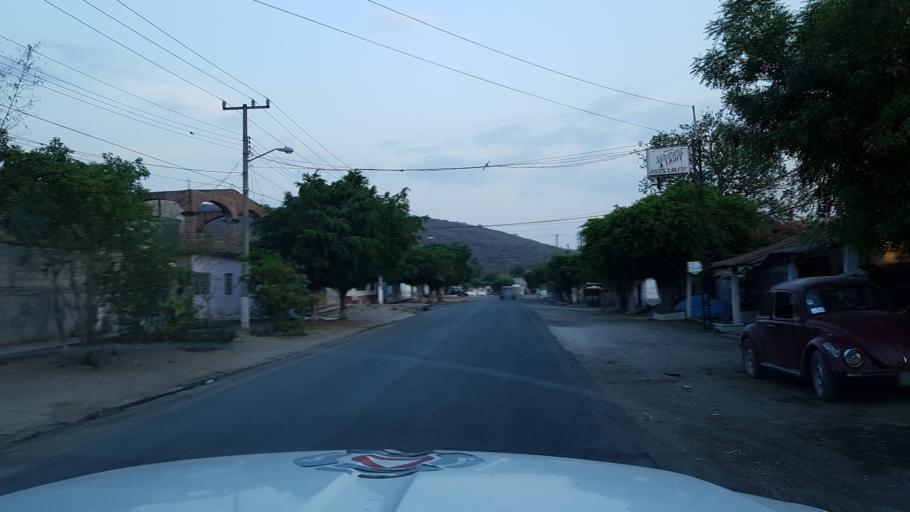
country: MX
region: Morelos
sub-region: Tlaltizapan de Zapata
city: Colonia Palo Prieto (Chipitongo)
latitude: 18.7126
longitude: -99.1088
